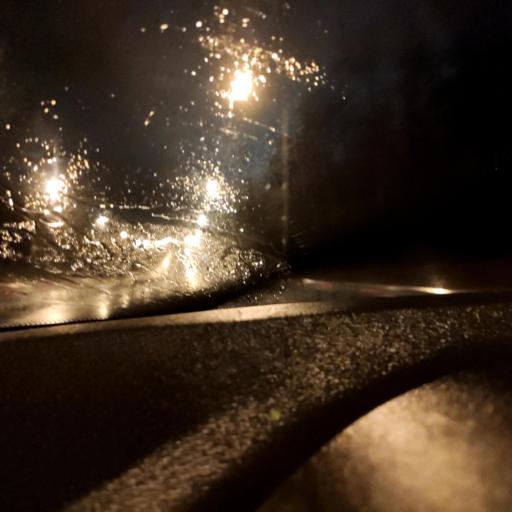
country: RU
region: Samara
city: Petra-Dubrava
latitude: 53.2906
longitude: 50.2480
